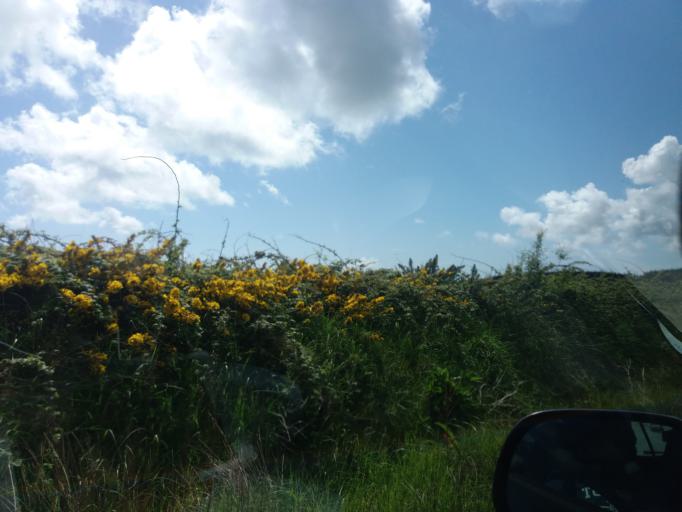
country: IE
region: Munster
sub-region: Waterford
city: Dunmore East
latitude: 52.2100
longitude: -6.8982
